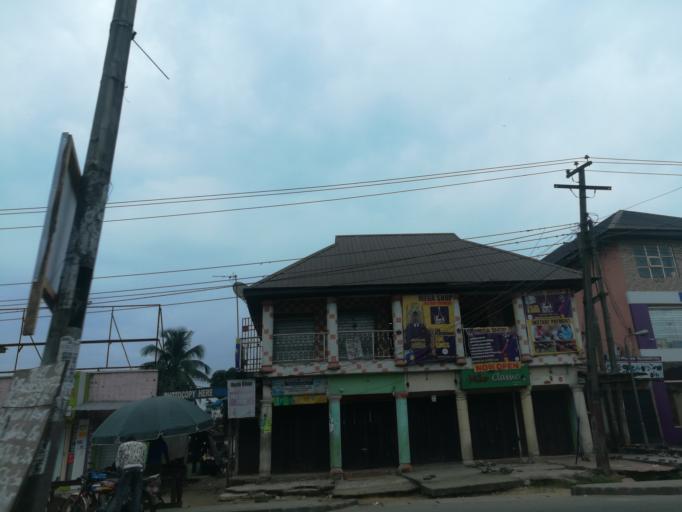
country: NG
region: Rivers
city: Port Harcourt
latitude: 4.8396
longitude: 6.9876
